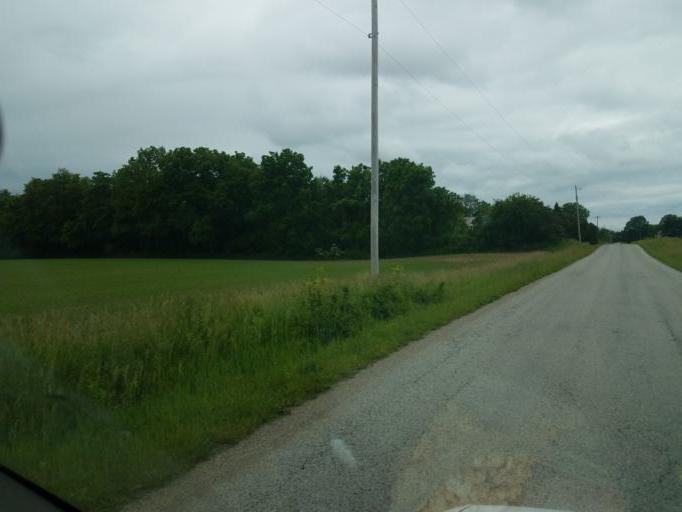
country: US
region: Ohio
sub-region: Morrow County
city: Cardington
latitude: 40.5284
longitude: -82.9233
